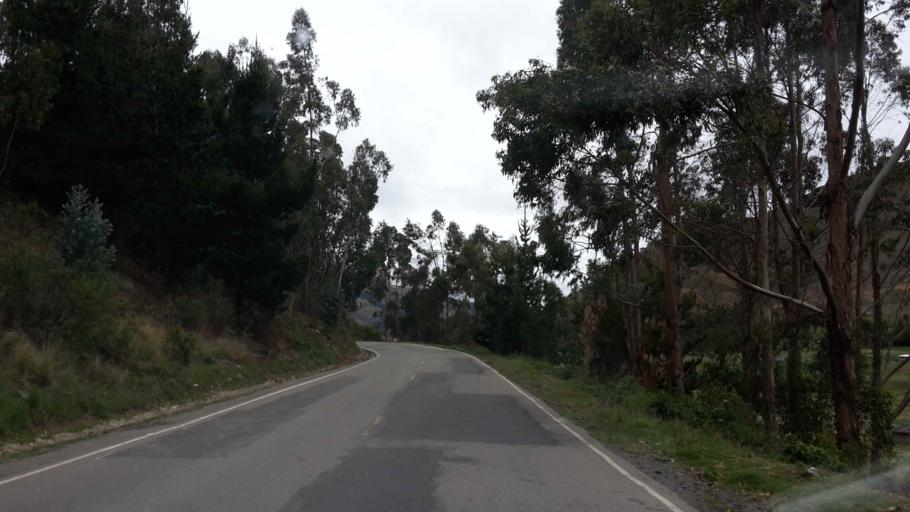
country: BO
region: Cochabamba
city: Arani
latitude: -17.4780
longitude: -65.5352
